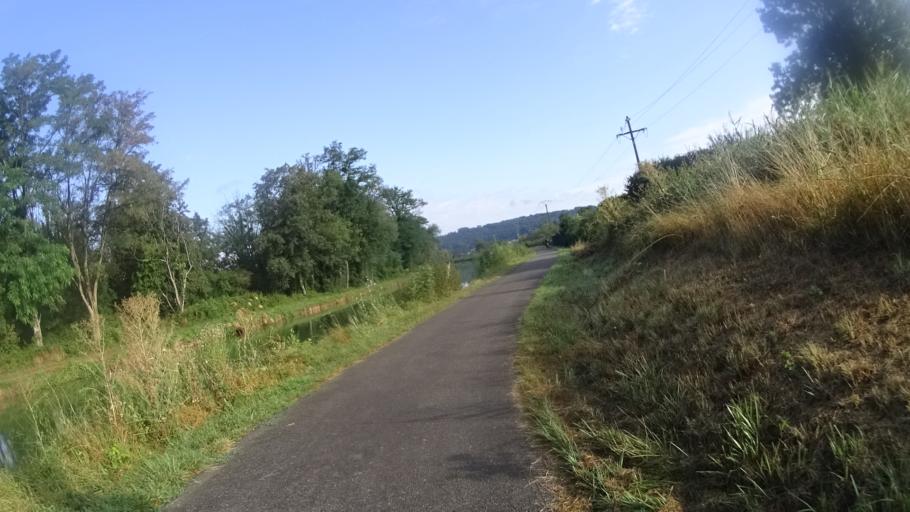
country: FR
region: Franche-Comte
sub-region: Departement du Doubs
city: Boussieres
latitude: 47.1562
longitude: 5.8566
